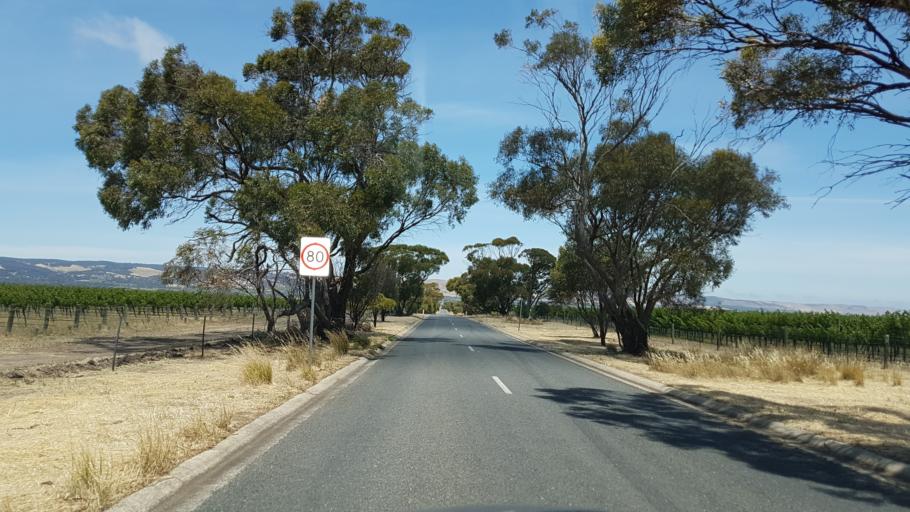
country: AU
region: South Australia
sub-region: Onkaparinga
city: McLaren Vale
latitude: -35.2327
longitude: 138.5192
